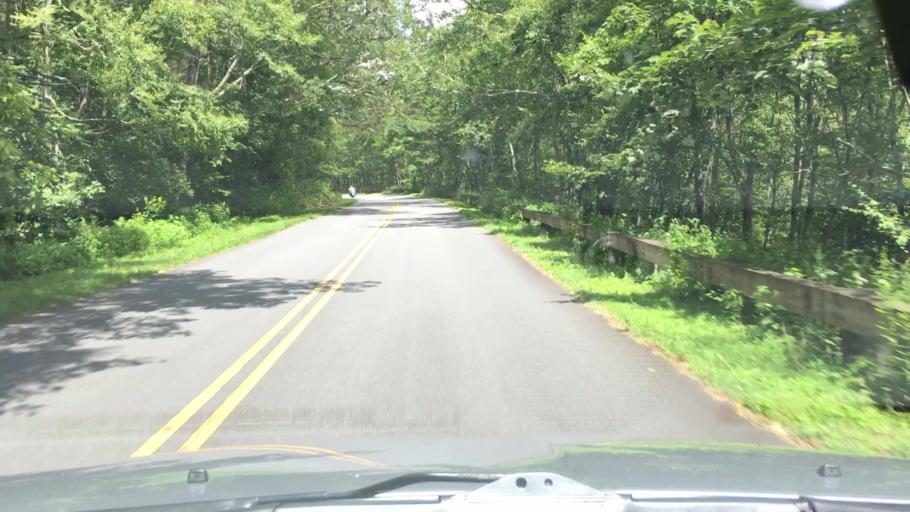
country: US
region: North Carolina
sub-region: Buncombe County
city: Swannanoa
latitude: 35.6870
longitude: -82.4102
